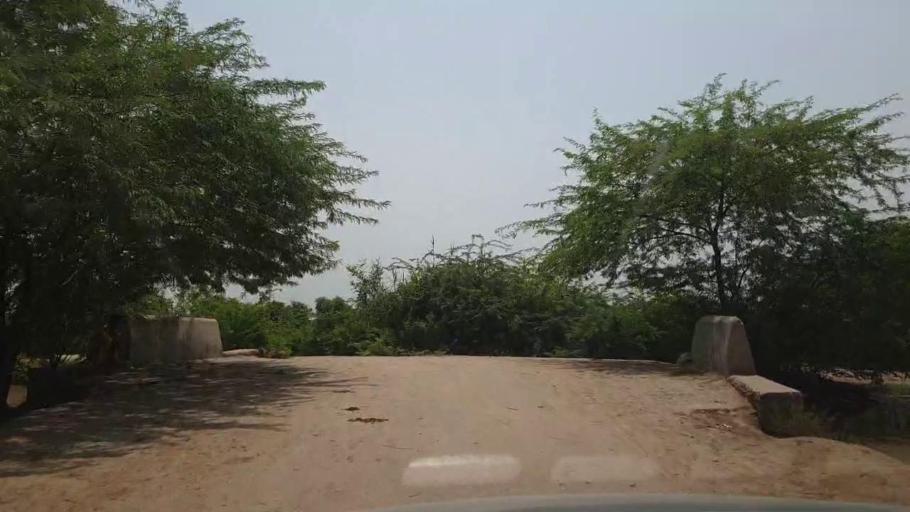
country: PK
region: Sindh
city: Garhi Yasin
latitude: 27.8768
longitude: 68.4954
